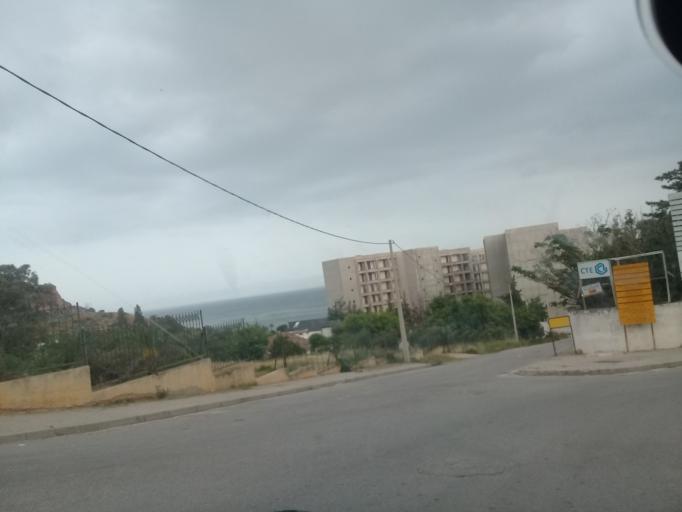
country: TN
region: Tunis
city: Sidi Bou Said
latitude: 36.8660
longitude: 10.3393
